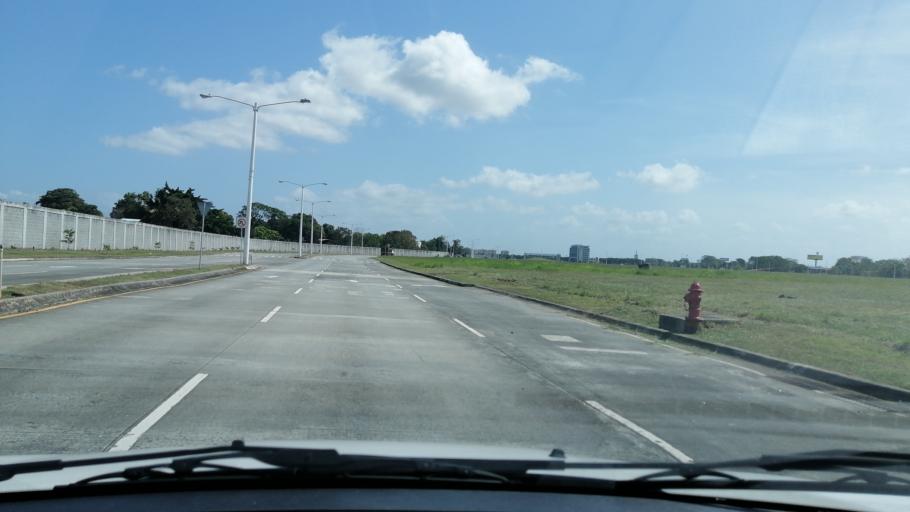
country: PA
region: Panama
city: San Miguelito
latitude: 9.0375
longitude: -79.4382
